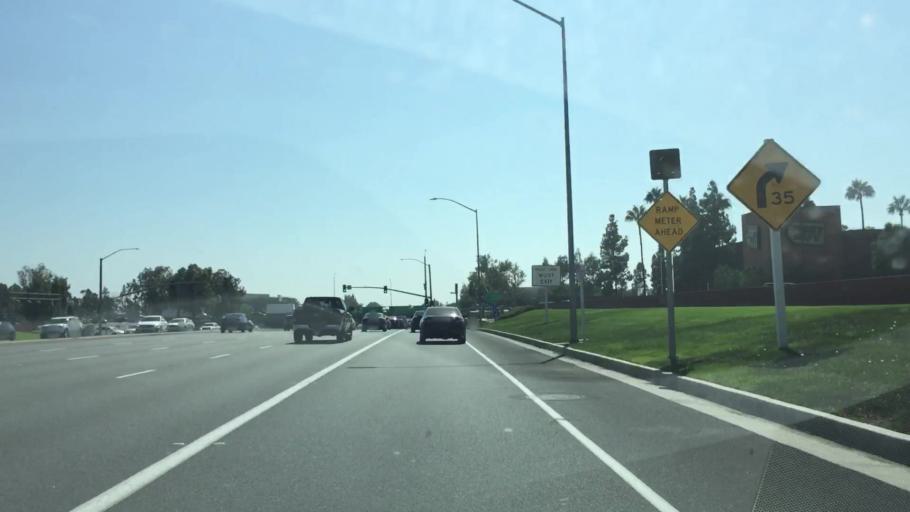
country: US
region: California
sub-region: Orange County
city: Tustin
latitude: 33.7218
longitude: -117.7932
